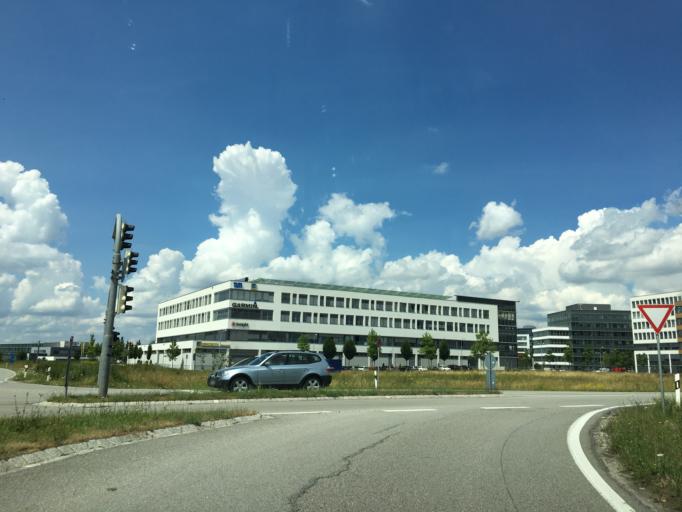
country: DE
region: Bavaria
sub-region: Upper Bavaria
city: Garching bei Munchen
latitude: 48.2481
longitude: 11.6349
